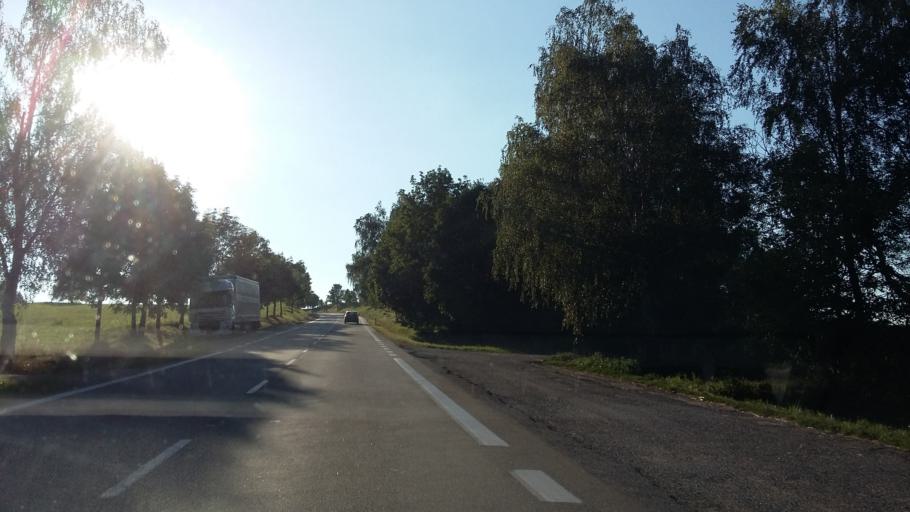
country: CZ
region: Vysocina
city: Merin
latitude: 49.3999
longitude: 15.8553
